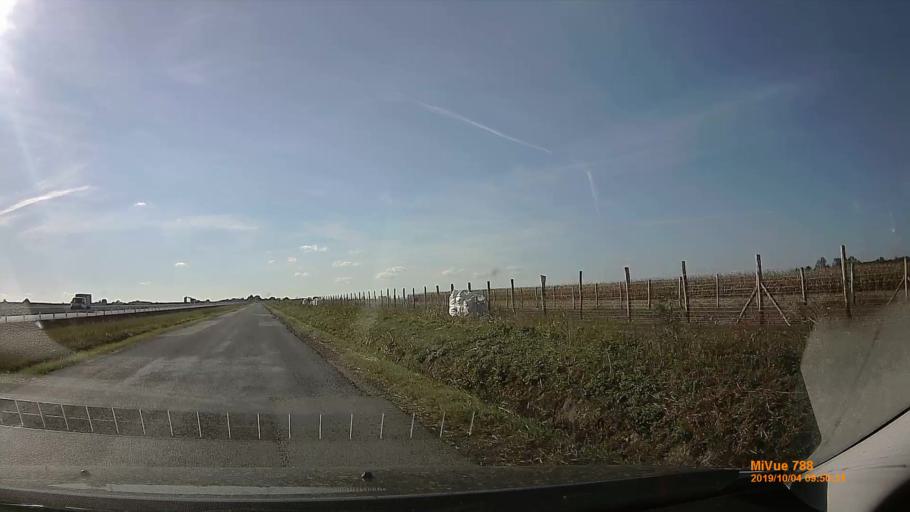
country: HU
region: Somogy
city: Kaposvar
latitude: 46.4349
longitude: 17.7716
